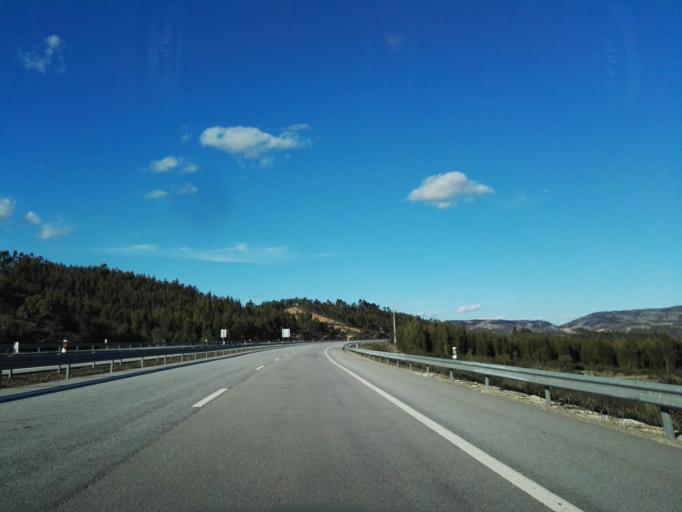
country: PT
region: Portalegre
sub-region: Nisa
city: Nisa
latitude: 39.6450
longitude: -7.7437
